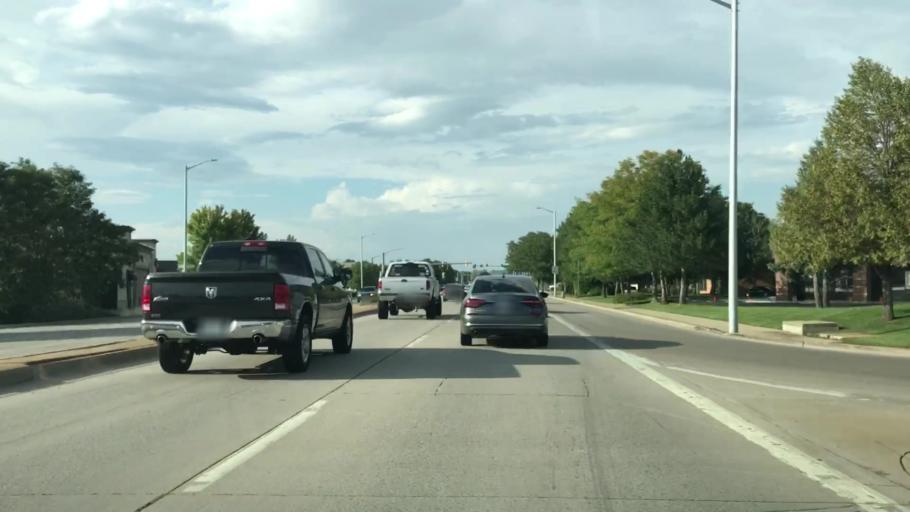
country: US
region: Colorado
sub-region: Boulder County
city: Longmont
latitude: 40.1423
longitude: -105.1307
